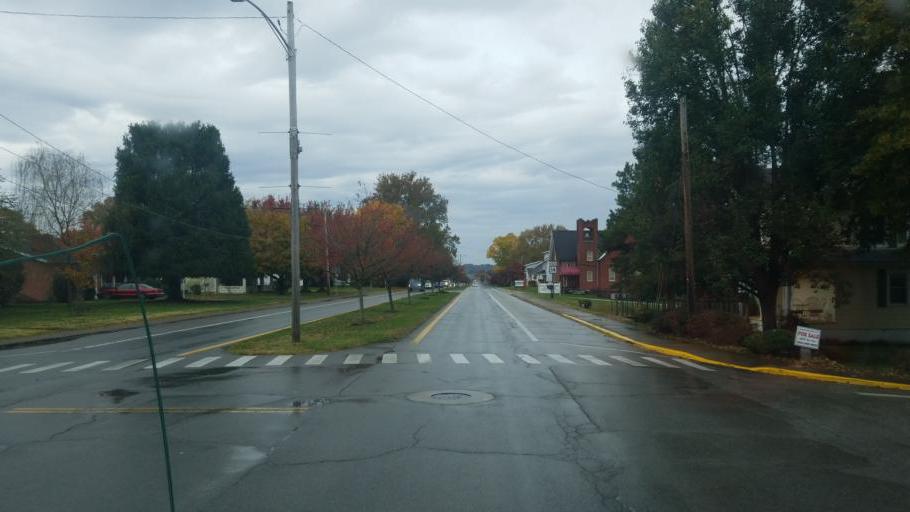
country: US
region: West Virginia
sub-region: Wood County
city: Vienna
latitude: 39.3327
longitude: -81.5450
